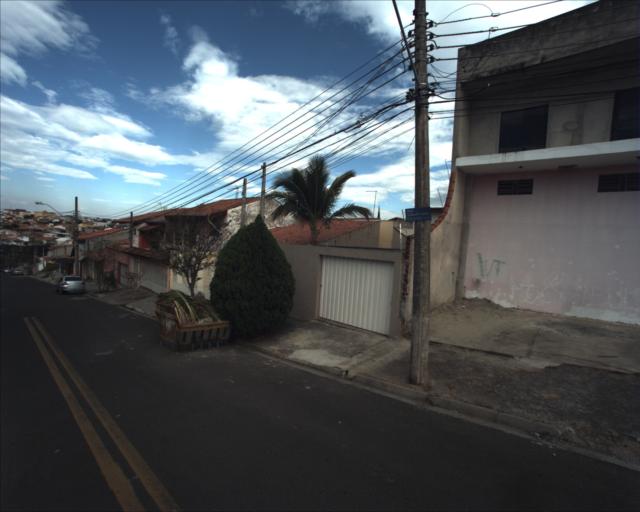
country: BR
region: Sao Paulo
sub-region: Sorocaba
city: Sorocaba
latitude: -23.4882
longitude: -47.5108
